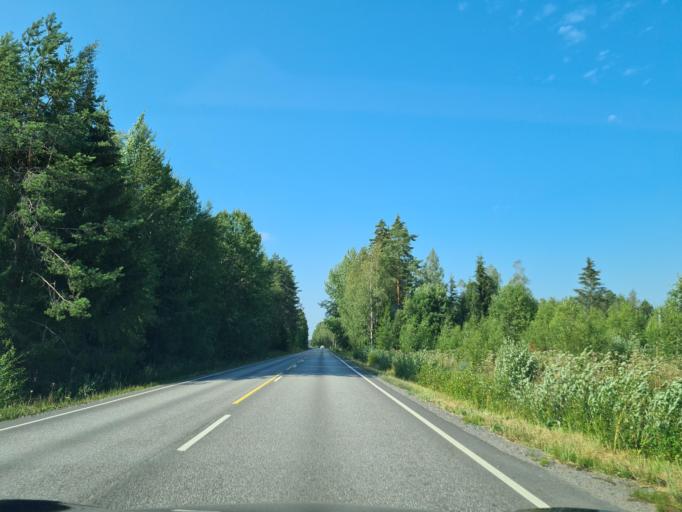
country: FI
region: Satakunta
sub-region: Pohjois-Satakunta
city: Kankaanpaeae
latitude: 61.9445
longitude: 22.5125
